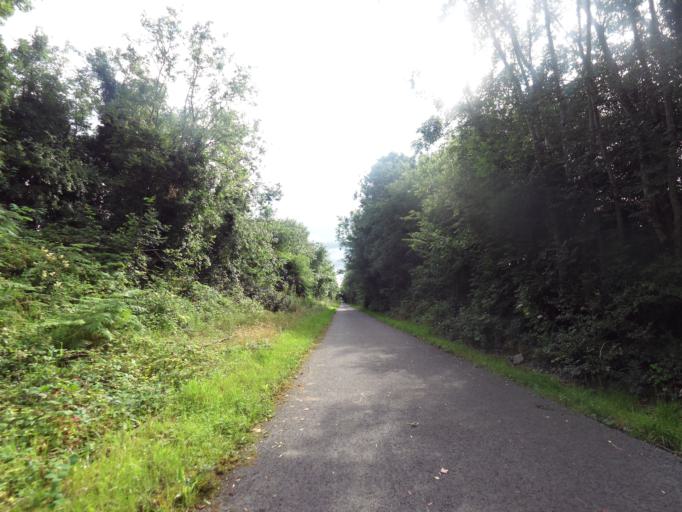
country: IE
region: Leinster
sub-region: An Iarmhi
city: An Muileann gCearr
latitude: 53.4998
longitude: -7.4368
